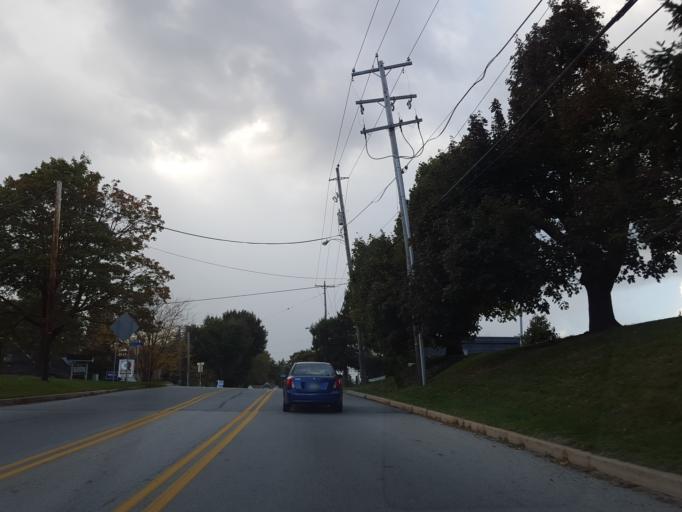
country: US
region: Pennsylvania
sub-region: York County
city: Valley View
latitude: 39.9402
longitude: -76.6970
